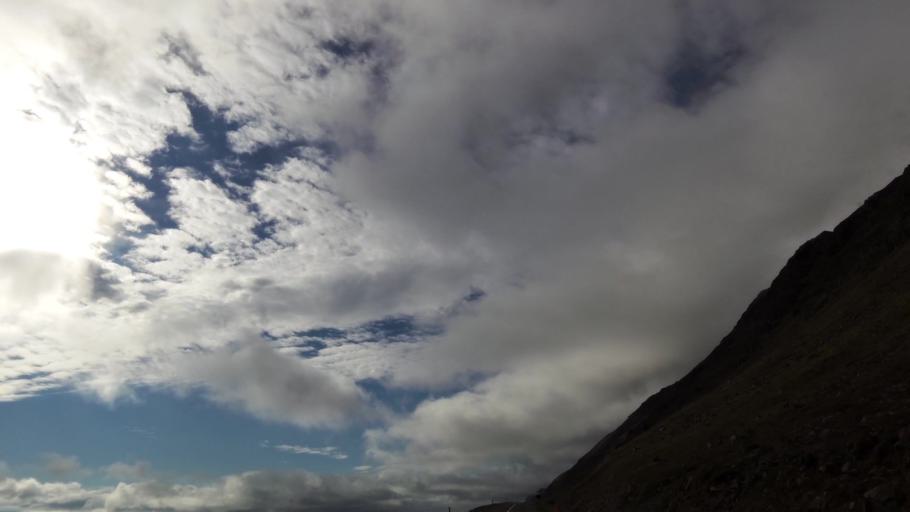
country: IS
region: West
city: Olafsvik
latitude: 65.5553
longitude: -23.8979
